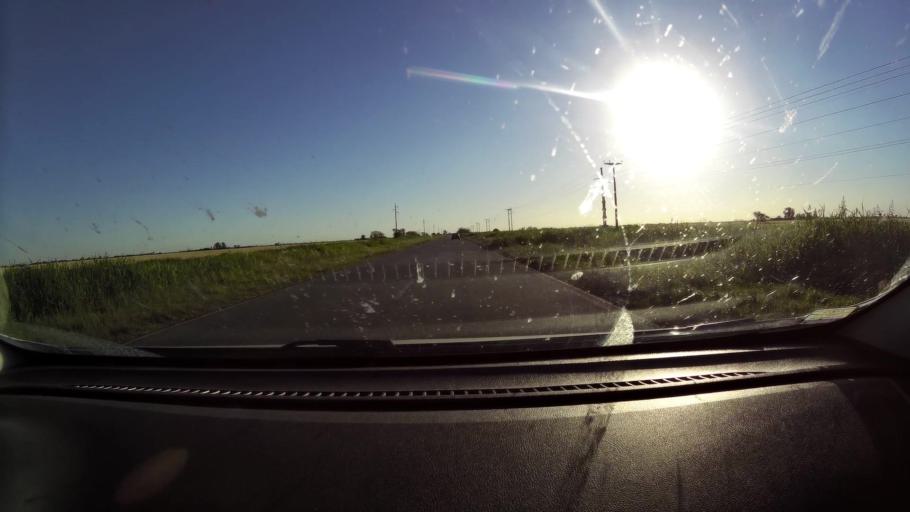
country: AR
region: Cordoba
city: Saturnino M. Laspiur
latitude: -31.7478
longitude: -62.5463
